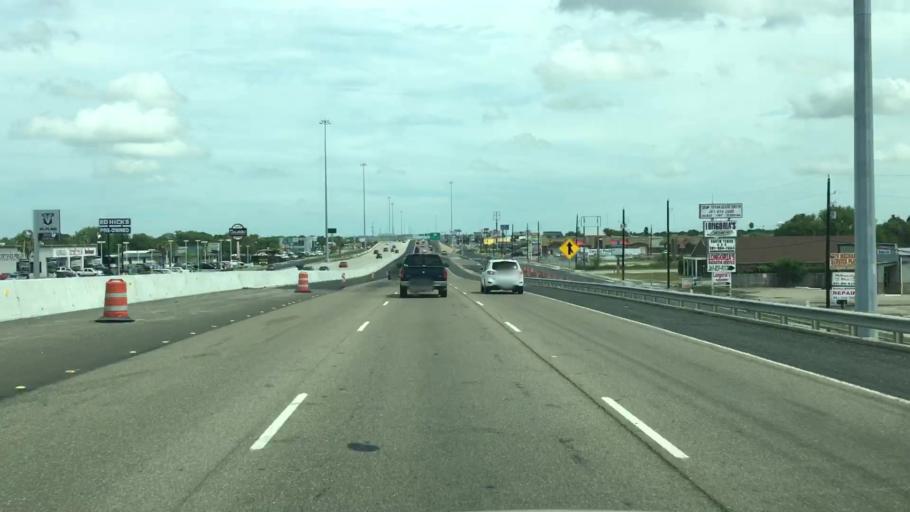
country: US
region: Texas
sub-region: Nueces County
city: Corpus Christi
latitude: 27.7280
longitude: -97.4120
